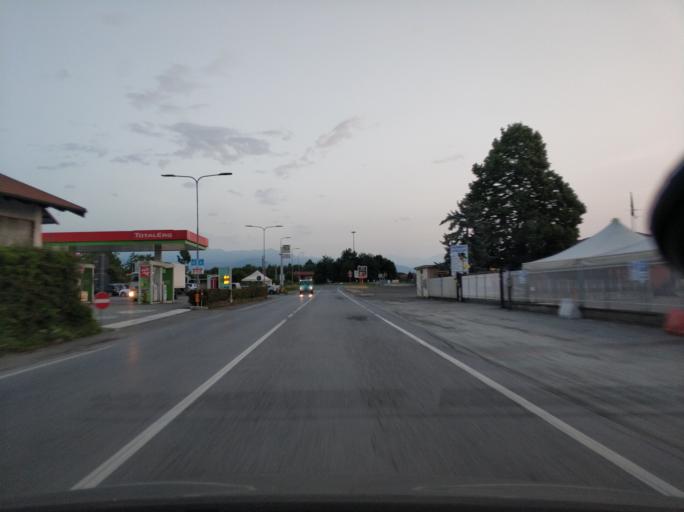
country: IT
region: Piedmont
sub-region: Provincia di Torino
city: San Maurizio
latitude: 45.2035
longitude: 7.6371
